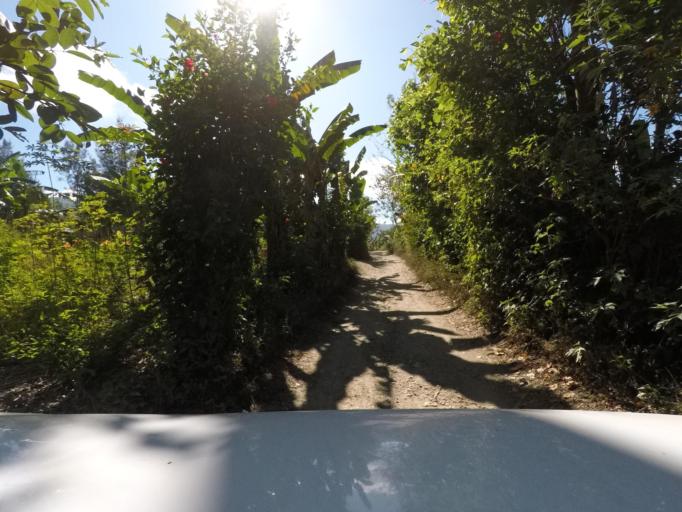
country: TL
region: Ermera
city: Gleno
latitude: -8.7114
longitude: 125.4484
